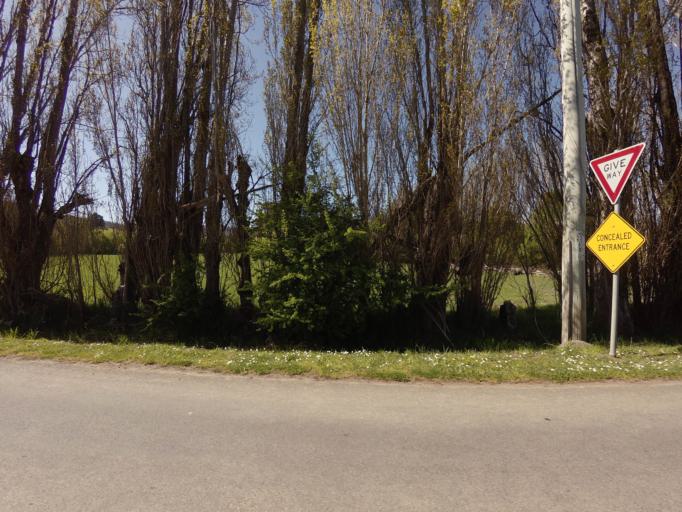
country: AU
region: Tasmania
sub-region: Derwent Valley
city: New Norfolk
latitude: -42.6736
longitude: 146.7899
